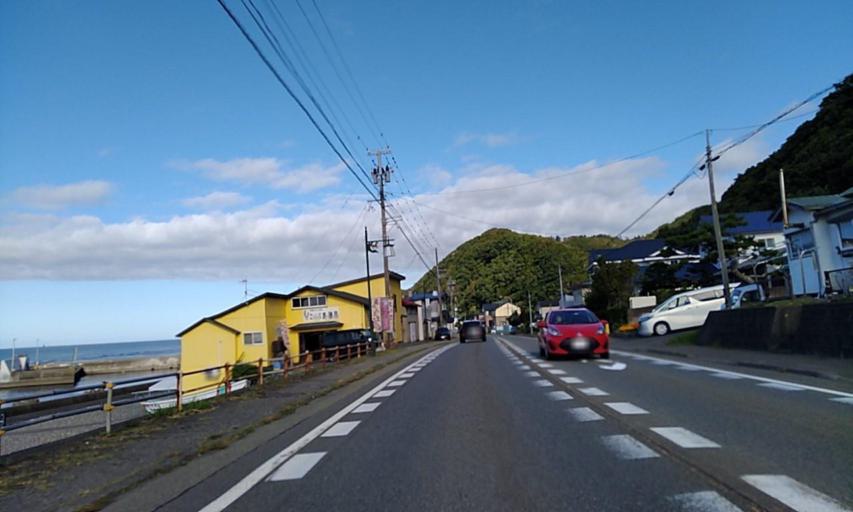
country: JP
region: Hokkaido
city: Shizunai-furukawacho
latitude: 42.2532
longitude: 142.5397
